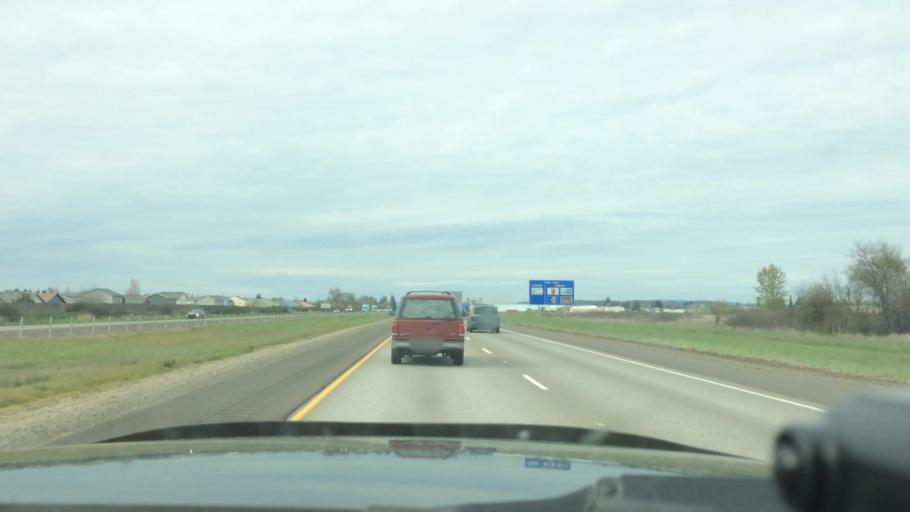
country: US
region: Oregon
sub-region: Linn County
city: Albany
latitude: 44.6140
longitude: -123.0619
